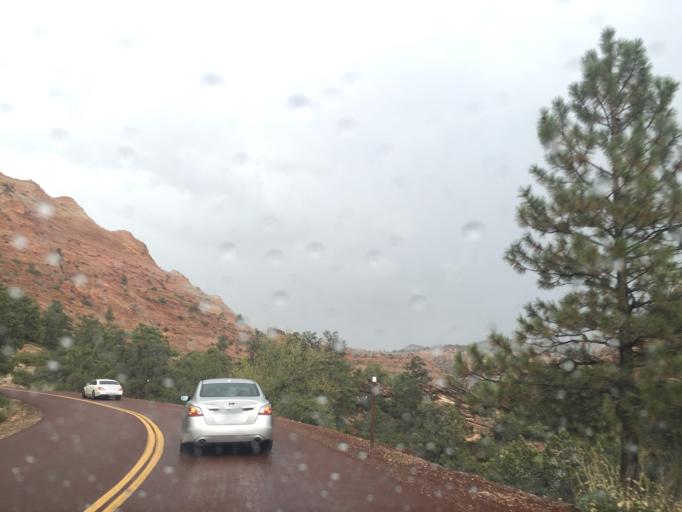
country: US
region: Utah
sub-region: Washington County
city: Hildale
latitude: 37.2159
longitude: -112.9296
